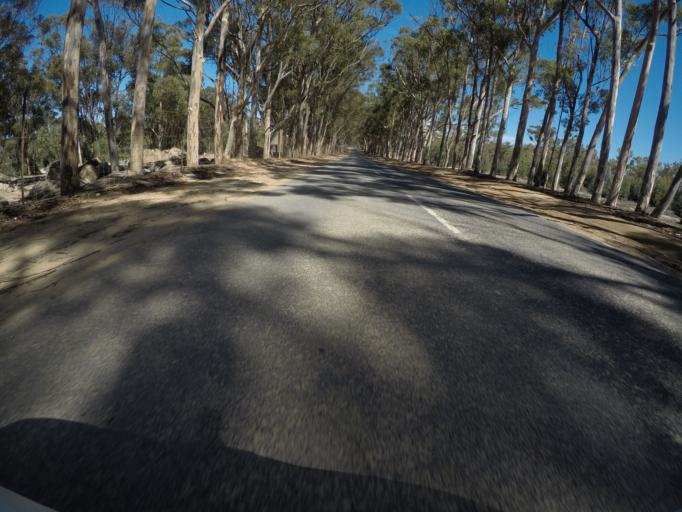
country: ZA
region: Western Cape
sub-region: City of Cape Town
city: Sunset Beach
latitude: -33.7645
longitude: 18.5509
